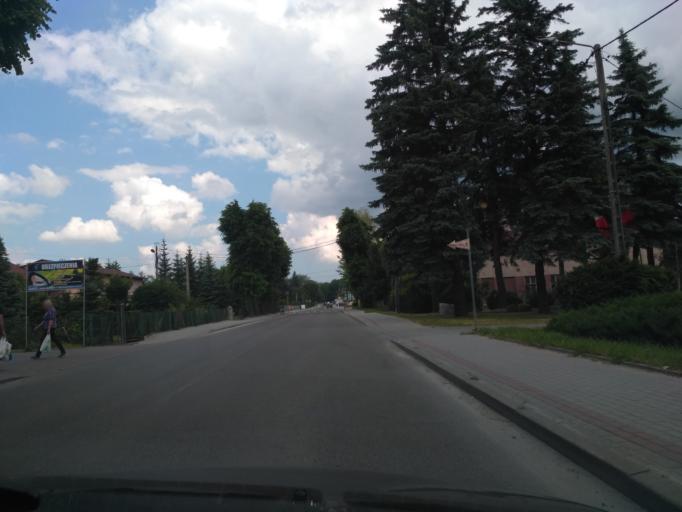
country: PL
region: Subcarpathian Voivodeship
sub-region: Powiat rzeszowski
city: Blazowa
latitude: 49.8865
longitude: 22.1006
